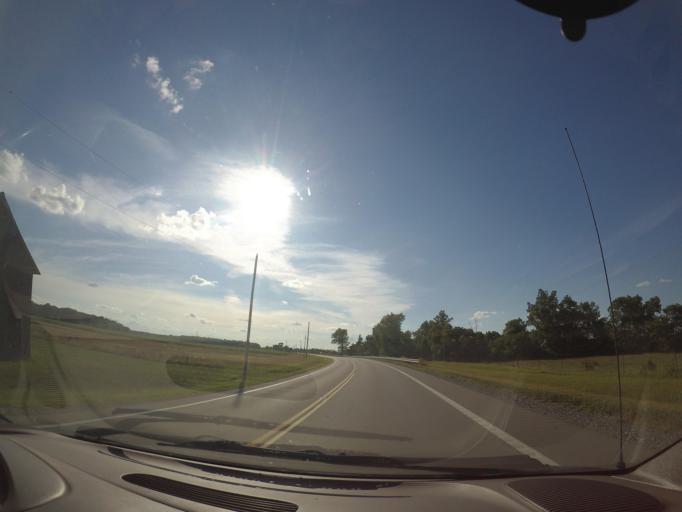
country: US
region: Ohio
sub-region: Henry County
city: Napoleon
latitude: 41.4293
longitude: -84.2060
